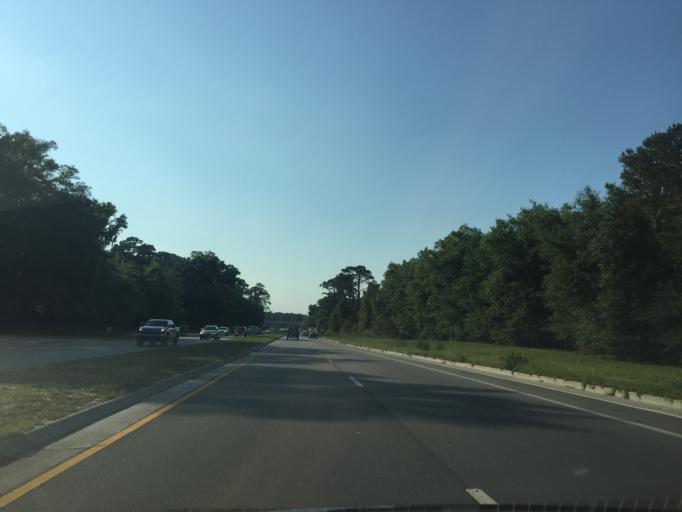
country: US
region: Georgia
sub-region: Chatham County
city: Montgomery
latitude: 31.9657
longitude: -81.1009
